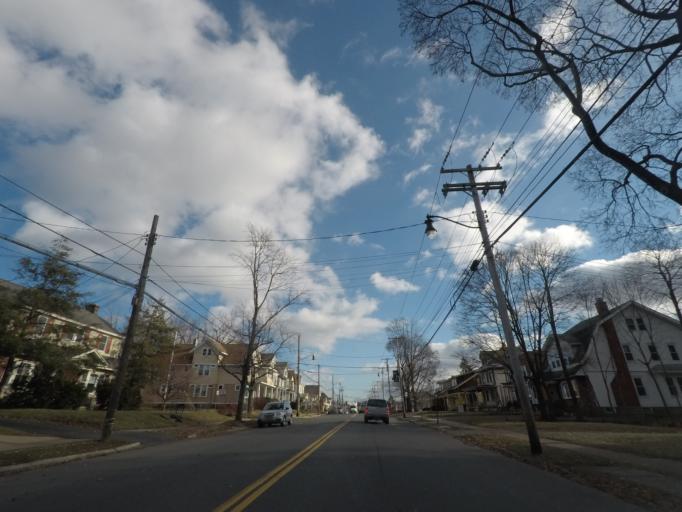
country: US
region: New York
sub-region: Schenectady County
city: Schenectady
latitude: 42.8058
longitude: -73.9074
